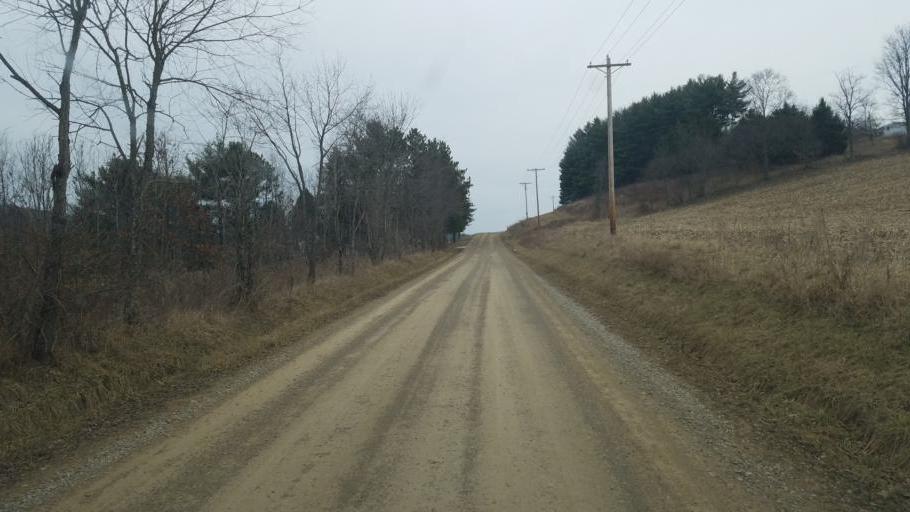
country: US
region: Ohio
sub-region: Knox County
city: Danville
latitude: 40.5363
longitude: -82.2793
